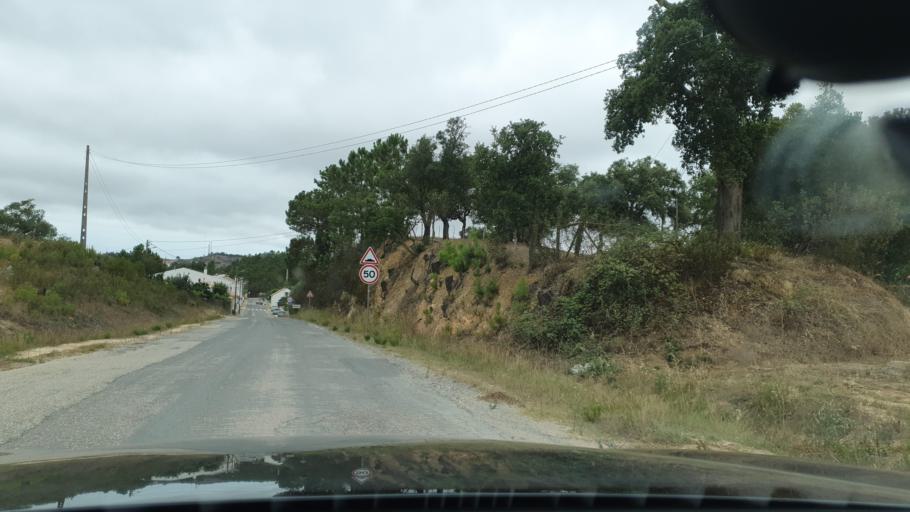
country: PT
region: Beja
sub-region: Odemira
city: Sao Teotonio
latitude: 37.5054
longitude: -8.6925
